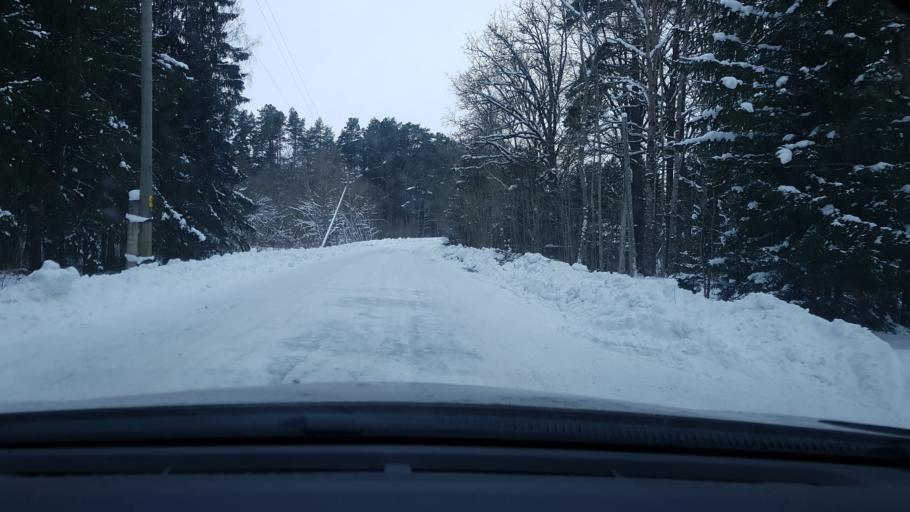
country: EE
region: Harju
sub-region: Keila linn
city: Keila
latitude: 59.3988
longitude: 24.4256
